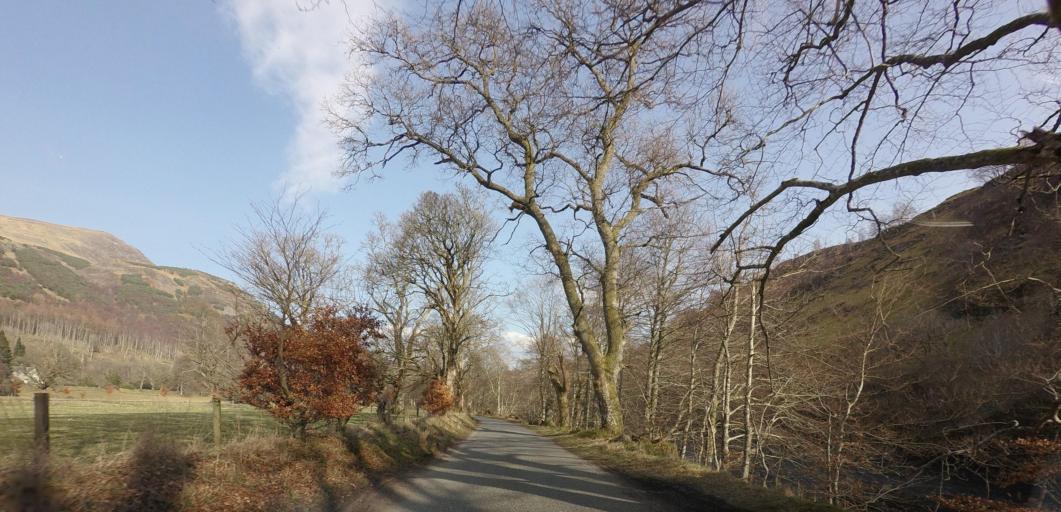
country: GB
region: Scotland
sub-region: Perth and Kinross
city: Comrie
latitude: 56.5988
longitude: -4.1285
